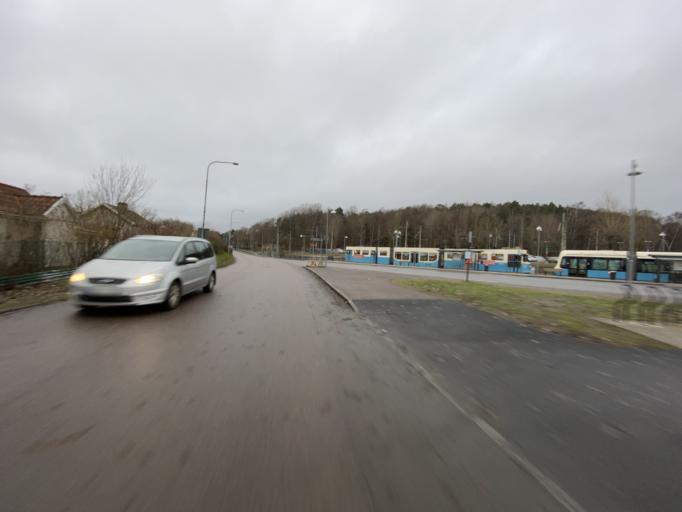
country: SE
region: Vaestra Goetaland
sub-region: Goteborg
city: Eriksbo
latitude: 57.7222
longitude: 12.0472
